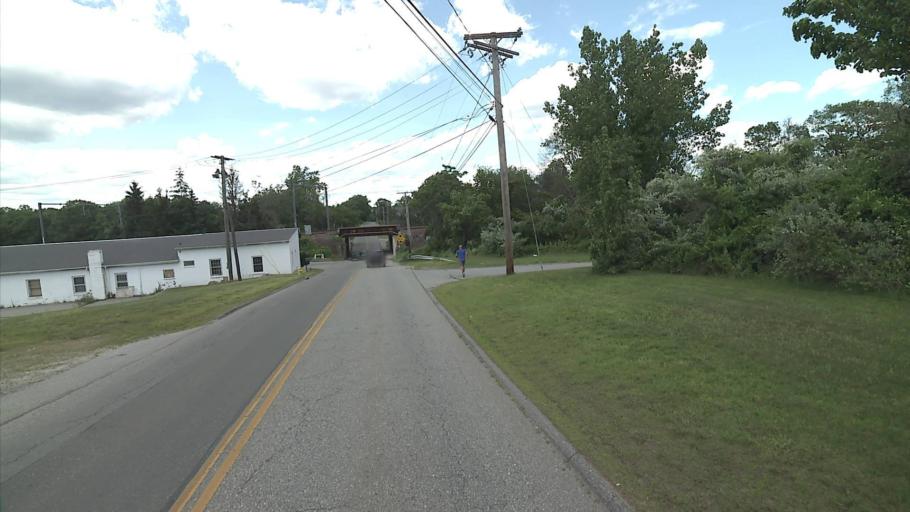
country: US
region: Connecticut
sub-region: New London County
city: Poquonock Bridge
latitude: 41.3411
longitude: -72.0389
